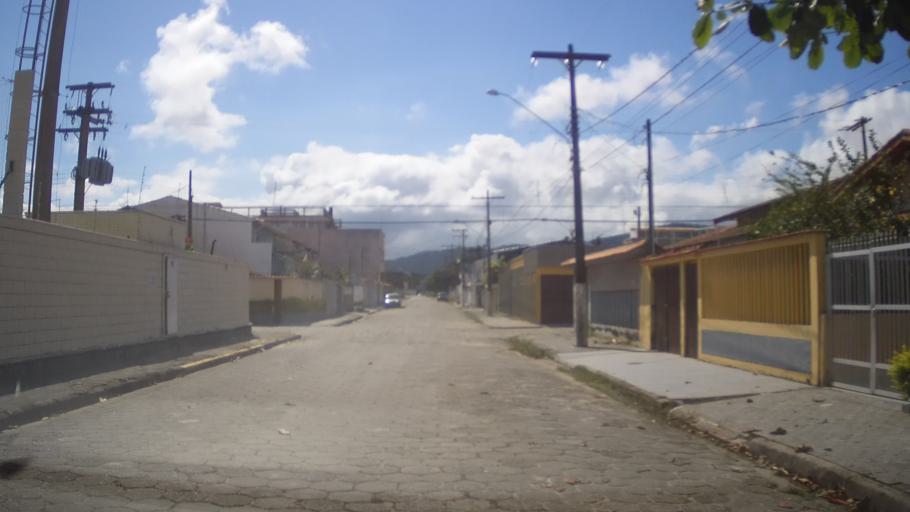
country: BR
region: Sao Paulo
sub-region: Itanhaem
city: Itanhaem
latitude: -24.1651
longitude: -46.7503
